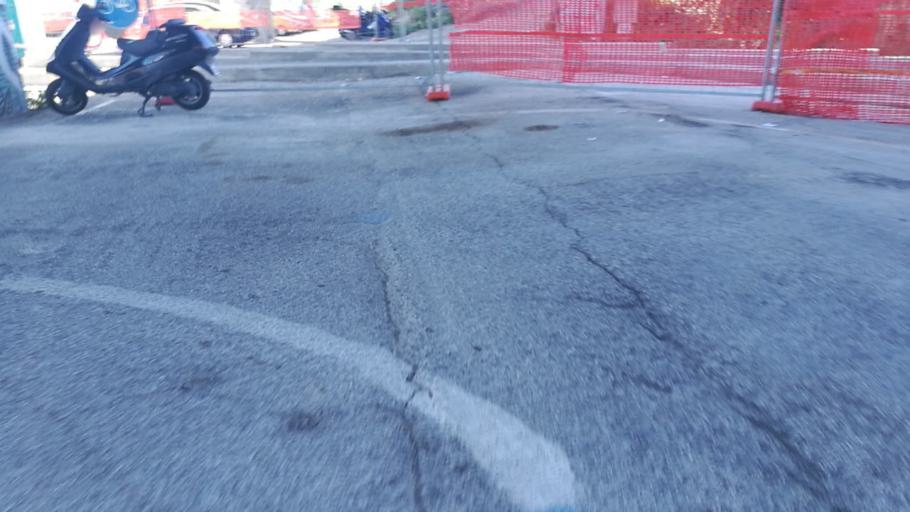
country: IT
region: Abruzzo
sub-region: Provincia di Chieti
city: Ortona
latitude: 42.3452
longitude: 14.4110
